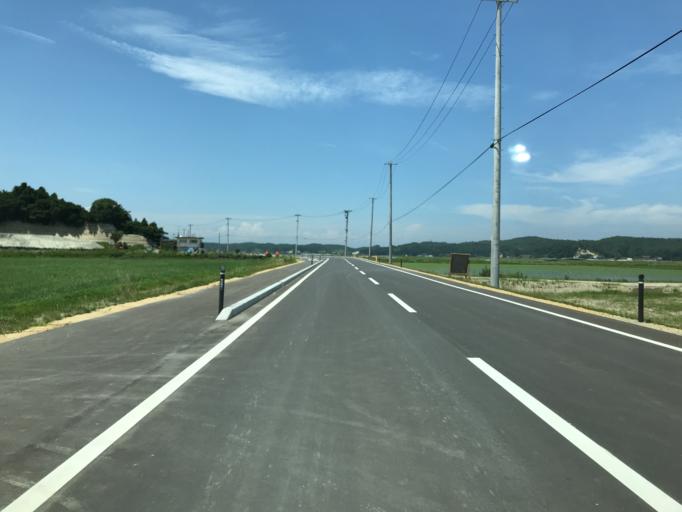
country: JP
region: Fukushima
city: Namie
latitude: 37.7203
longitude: 140.9980
